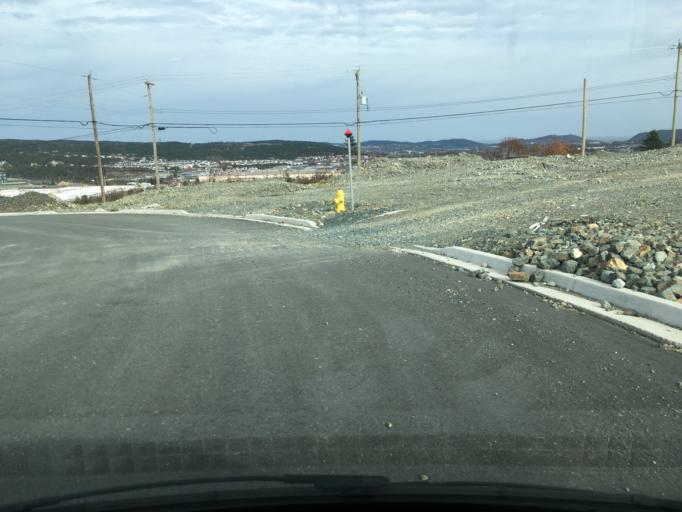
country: CA
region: Newfoundland and Labrador
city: Mount Pearl
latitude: 47.5526
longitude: -52.7860
